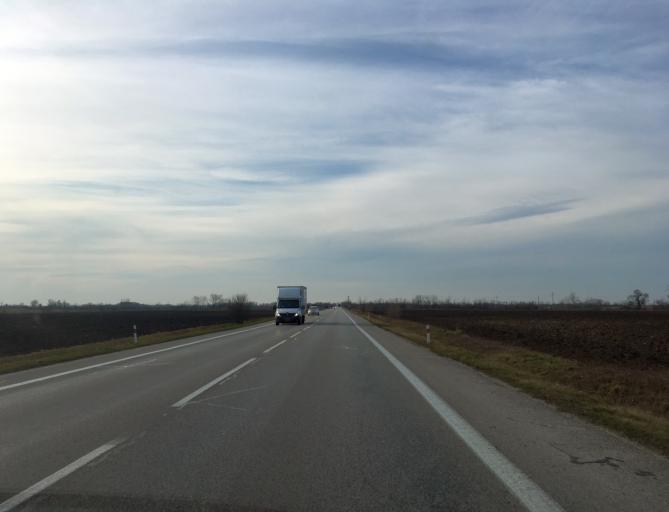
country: SK
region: Nitriansky
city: Sellye
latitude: 48.1410
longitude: 17.9925
